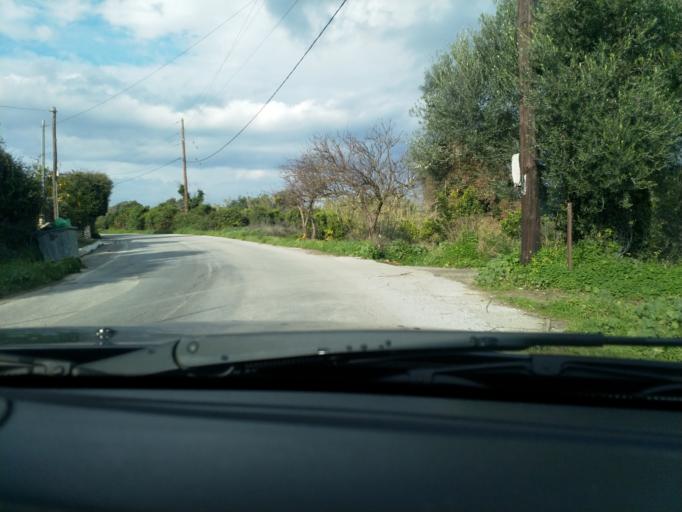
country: GR
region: Crete
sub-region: Nomos Chanias
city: Gerani
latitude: 35.5011
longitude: 23.8976
